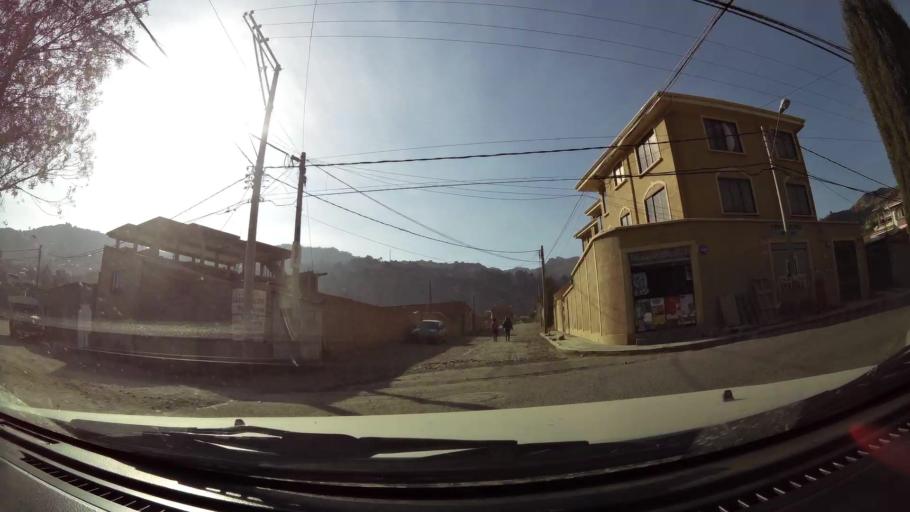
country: BO
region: La Paz
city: La Paz
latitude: -16.5015
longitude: -68.0835
